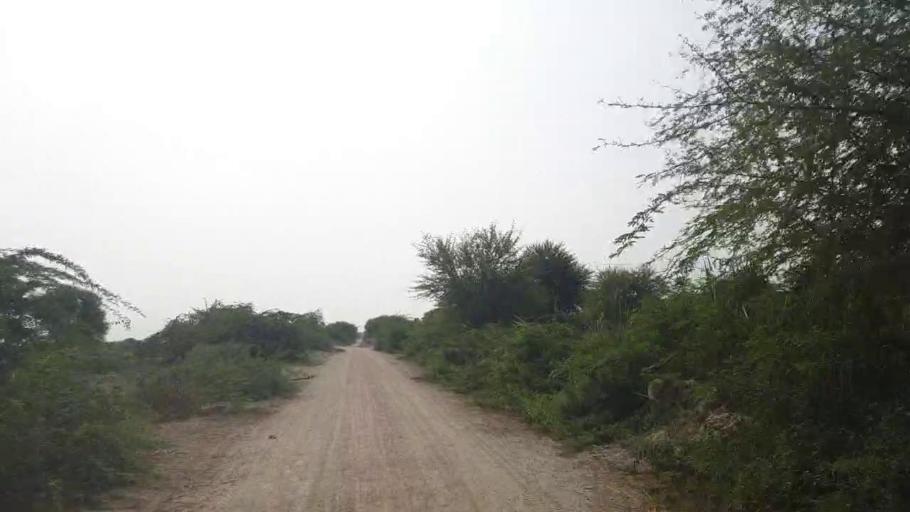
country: PK
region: Sindh
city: Badin
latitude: 24.6096
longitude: 68.7210
